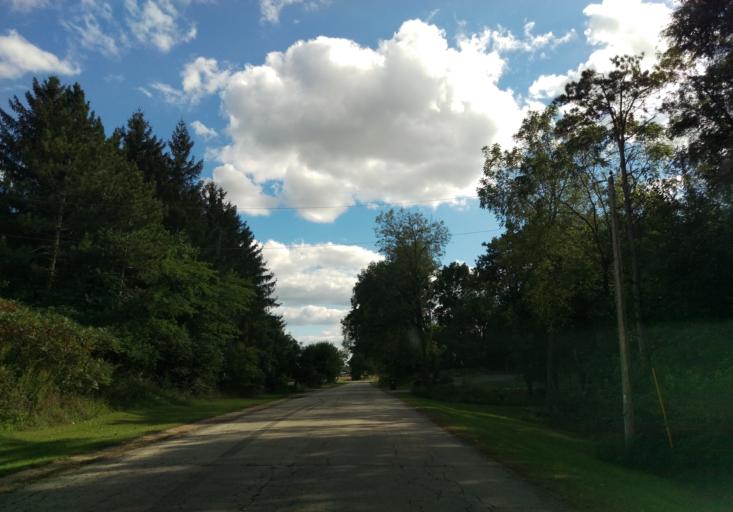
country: US
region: Wisconsin
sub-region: Rock County
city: Evansville
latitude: 42.7730
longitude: -89.2404
